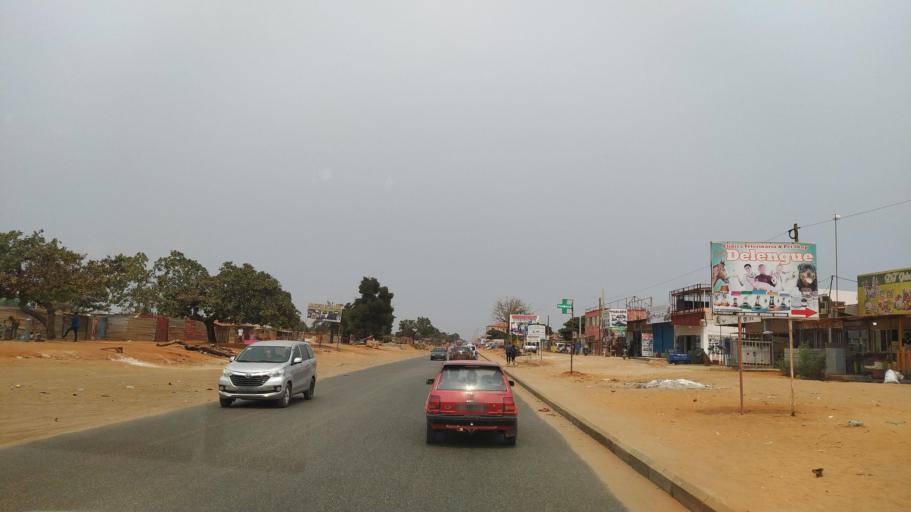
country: AO
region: Luanda
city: Luanda
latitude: -9.0566
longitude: 13.4137
